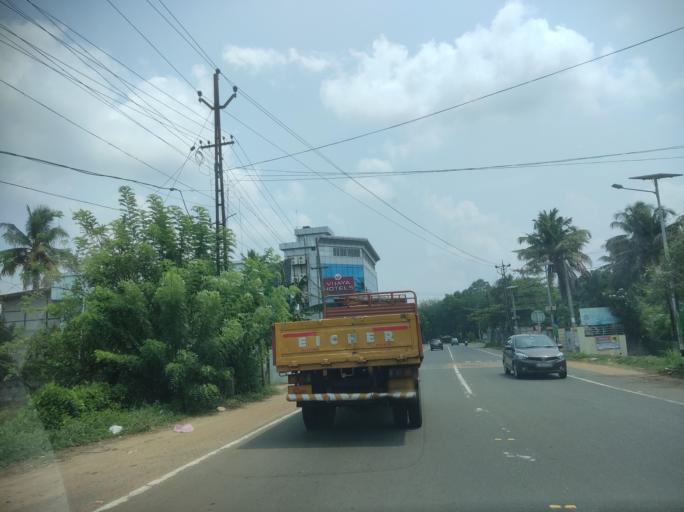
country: IN
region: Kerala
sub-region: Kottayam
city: Changanacheri
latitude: 9.4221
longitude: 76.5459
